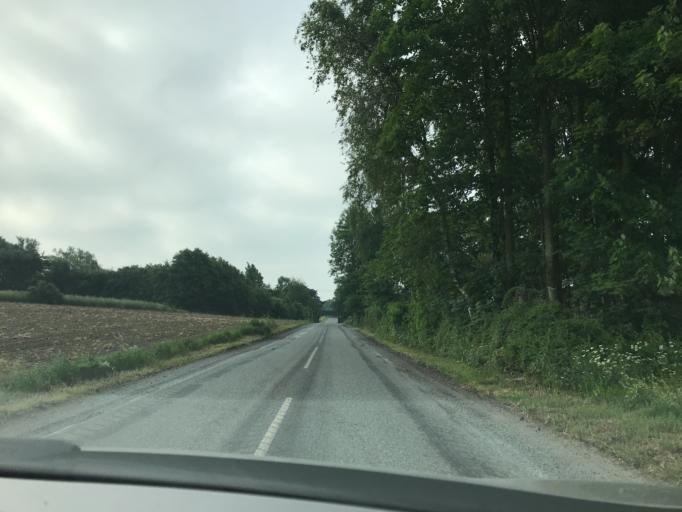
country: DK
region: South Denmark
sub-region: Odense Kommune
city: Bellinge
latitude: 55.3720
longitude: 10.2953
